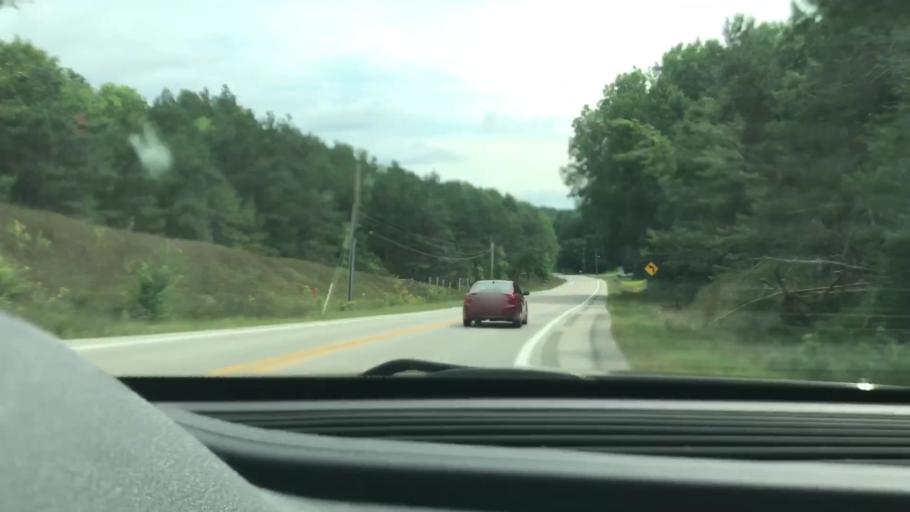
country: US
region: Michigan
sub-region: Antrim County
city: Bellaire
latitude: 45.0846
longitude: -85.2862
